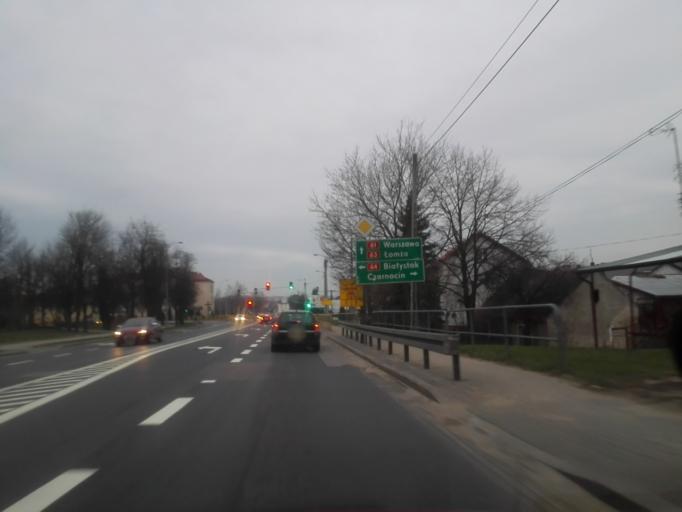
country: PL
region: Podlasie
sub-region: Powiat lomzynski
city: Piatnica
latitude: 53.1962
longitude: 22.0964
